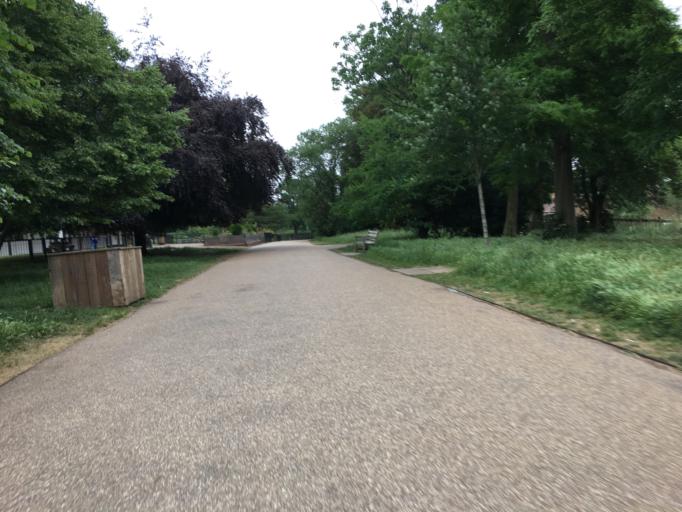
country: GB
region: England
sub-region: Greater London
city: Camden Town
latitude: 51.5589
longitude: -0.1531
